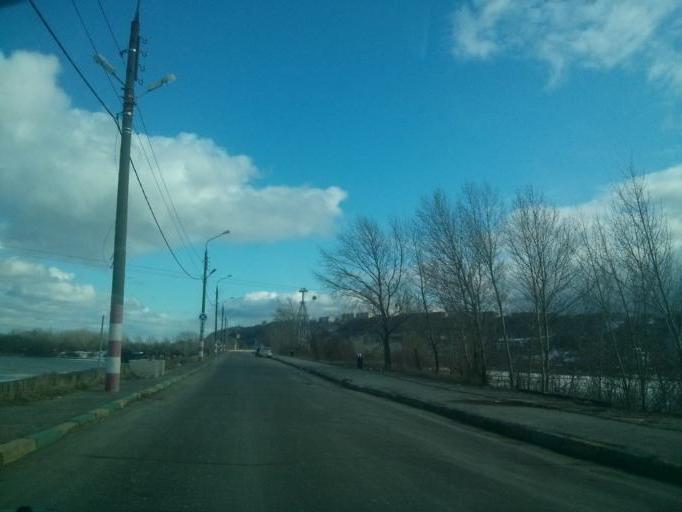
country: RU
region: Nizjnij Novgorod
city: Nizhniy Novgorod
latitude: 56.3322
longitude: 44.0395
